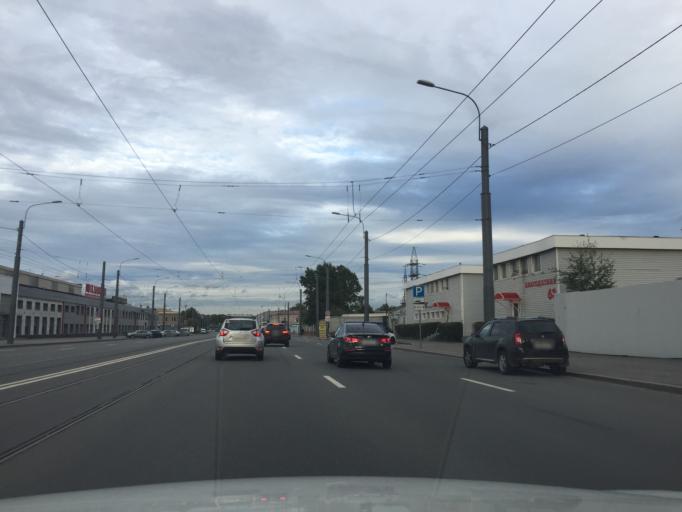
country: RU
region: St.-Petersburg
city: Kupchino
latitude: 59.8764
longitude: 30.3388
